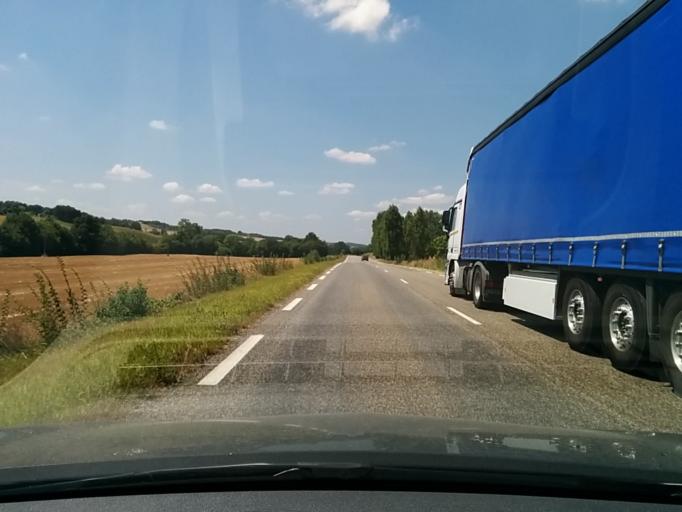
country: FR
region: Midi-Pyrenees
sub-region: Departement du Gers
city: Auch
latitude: 43.6800
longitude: 0.5026
